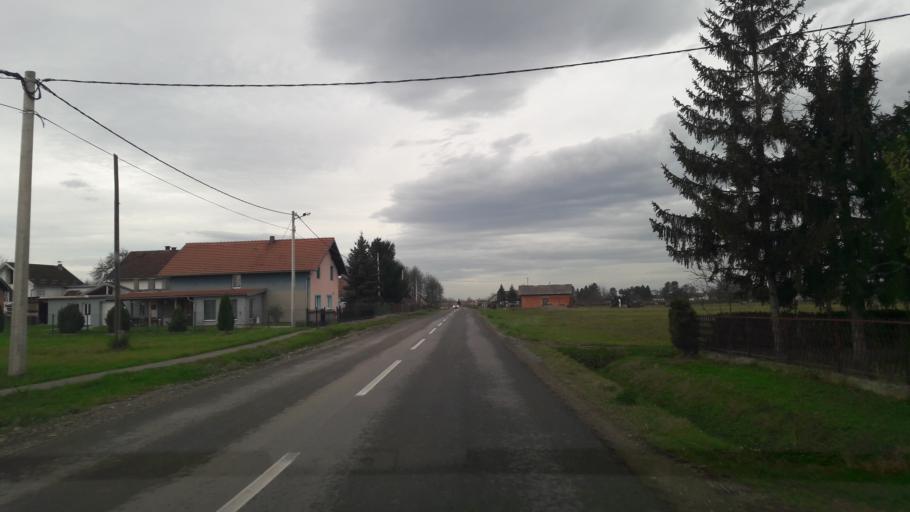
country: HR
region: Osjecko-Baranjska
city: Fericanci
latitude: 45.5317
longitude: 18.0261
